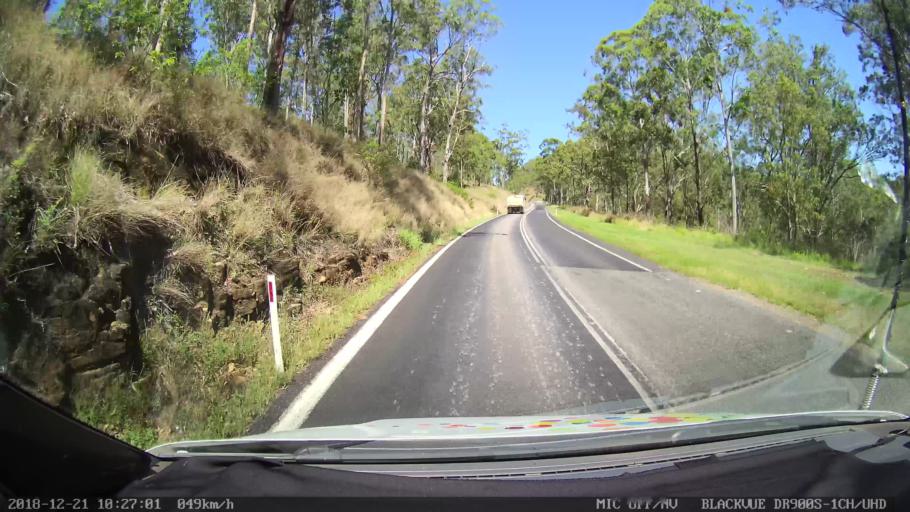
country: AU
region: New South Wales
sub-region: Clarence Valley
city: South Grafton
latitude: -29.6306
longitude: 152.7439
